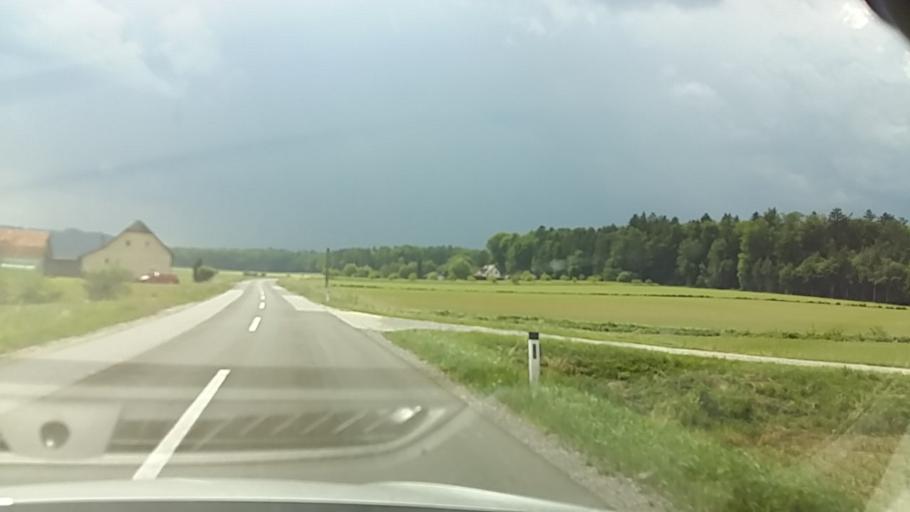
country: AT
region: Styria
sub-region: Politischer Bezirk Suedoststeiermark
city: Breitenfeld an der Rittschein
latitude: 47.0449
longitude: 15.9714
